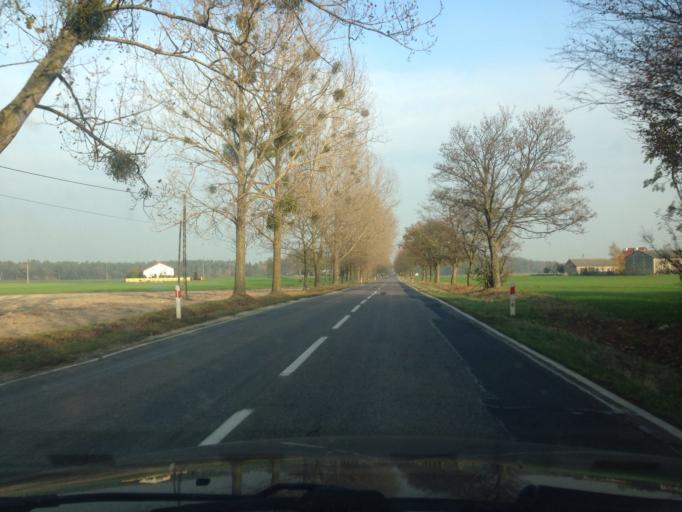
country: PL
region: Kujawsko-Pomorskie
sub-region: Powiat brodnicki
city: Bobrowo
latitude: 53.2276
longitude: 19.2146
